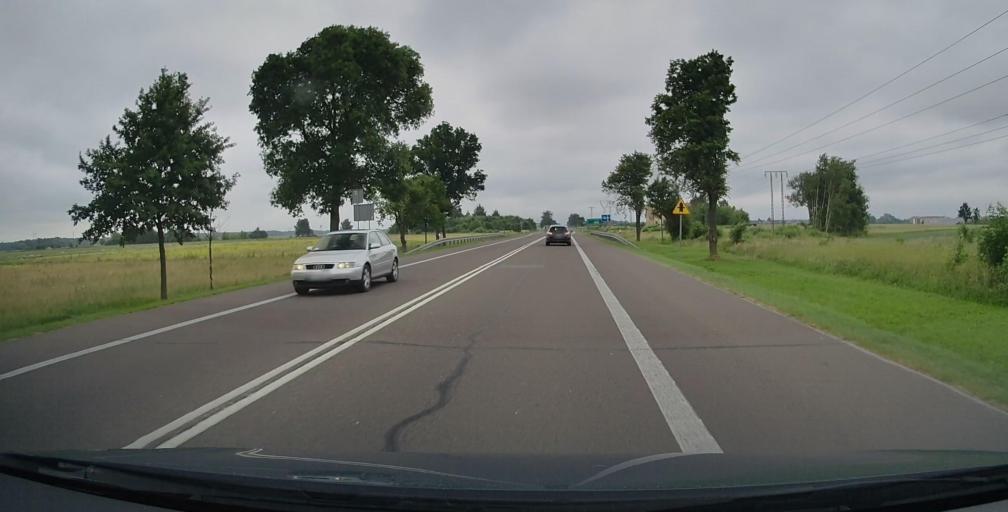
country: PL
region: Lublin Voivodeship
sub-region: Powiat bialski
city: Miedzyrzec Podlaski
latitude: 52.0002
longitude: 22.7799
